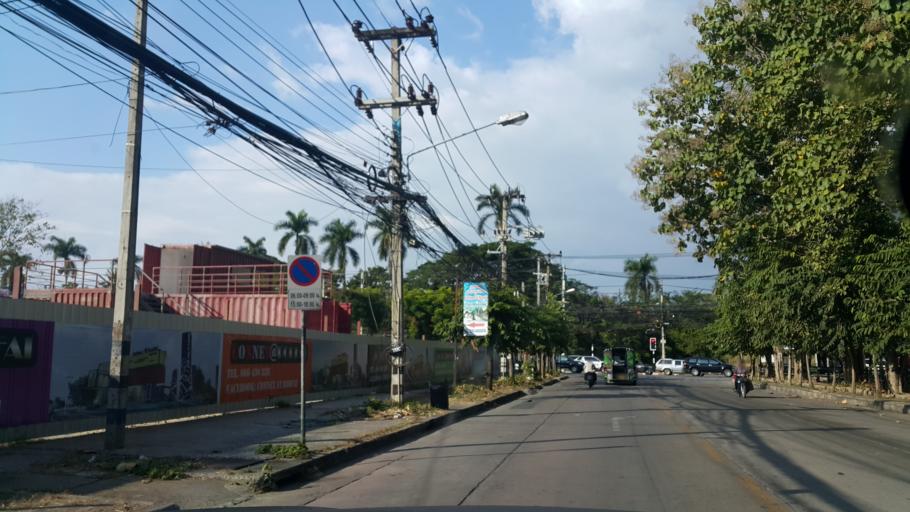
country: TH
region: Chiang Mai
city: Chiang Mai
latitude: 18.7848
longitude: 99.0163
